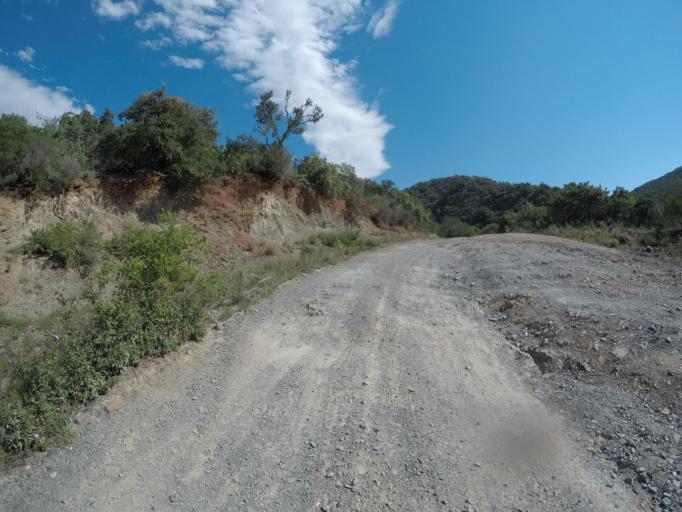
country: ZA
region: Eastern Cape
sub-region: Cacadu District Municipality
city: Kareedouw
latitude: -33.6573
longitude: 24.4270
